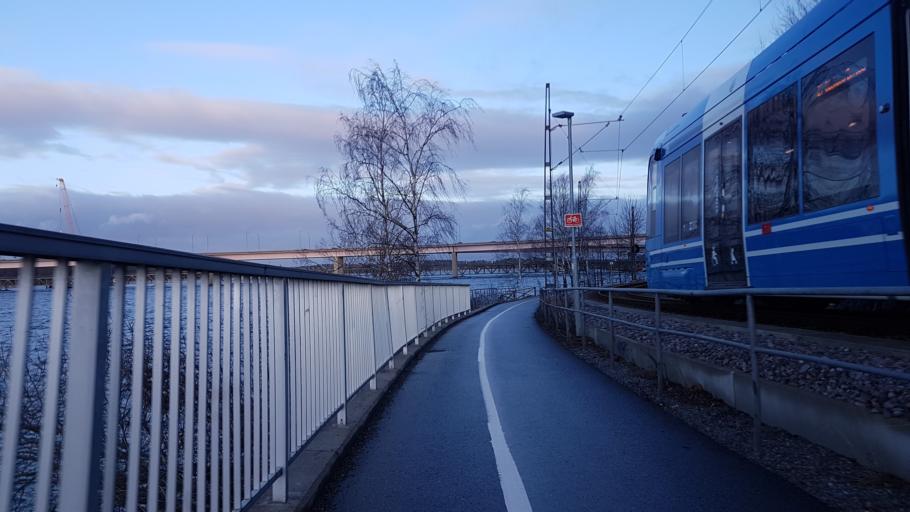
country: SE
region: Stockholm
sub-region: Lidingo
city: Lidingoe
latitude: 59.3592
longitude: 18.1186
